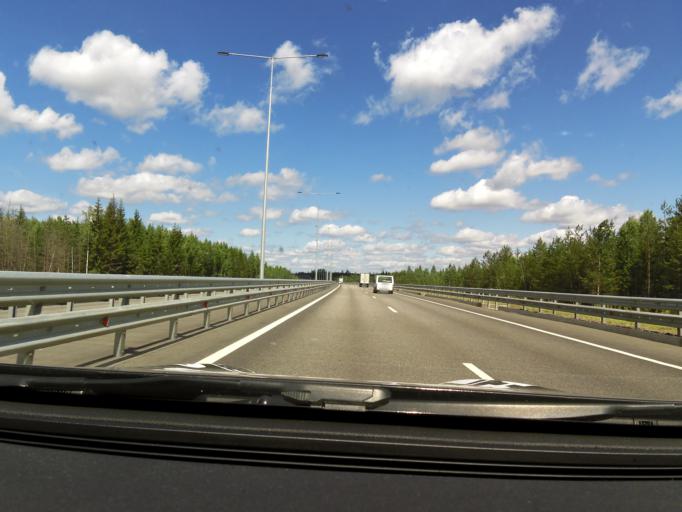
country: RU
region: Tverskaya
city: Krasnomayskiy
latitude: 57.6674
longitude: 34.2313
